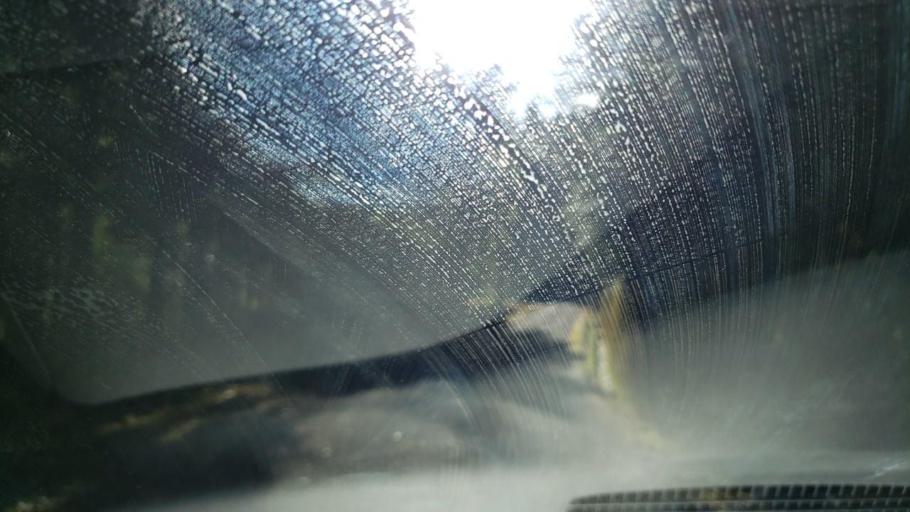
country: JP
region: Tokushima
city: Ikedacho
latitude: 33.9886
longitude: 133.9824
